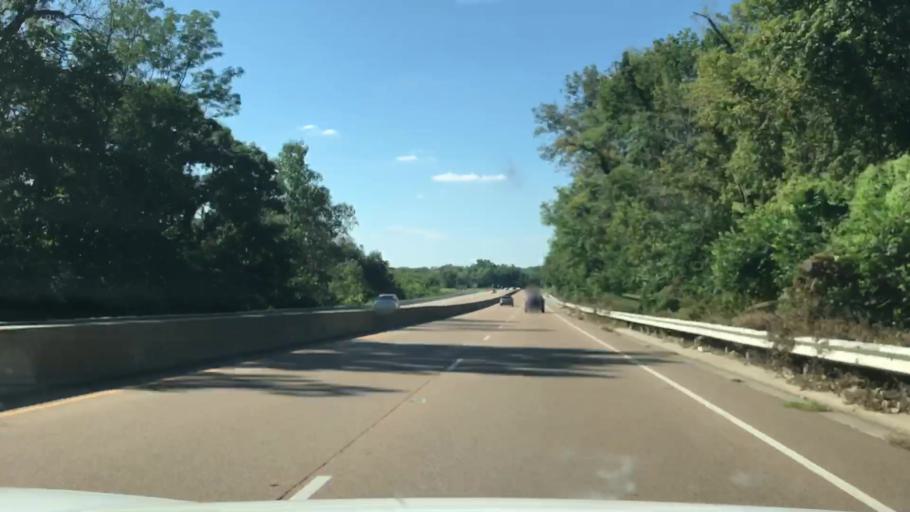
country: US
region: Illinois
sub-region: Saint Clair County
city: Alorton
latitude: 38.5525
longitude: -90.0734
